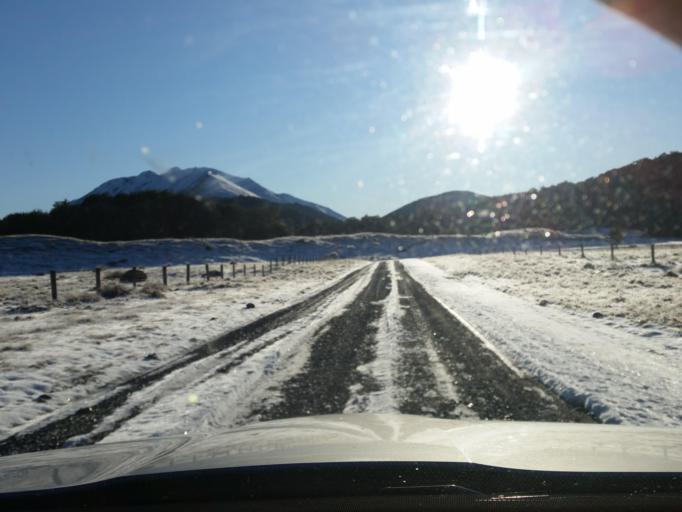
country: NZ
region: Southland
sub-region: Southland District
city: Te Anau
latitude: -45.3316
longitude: 168.1768
